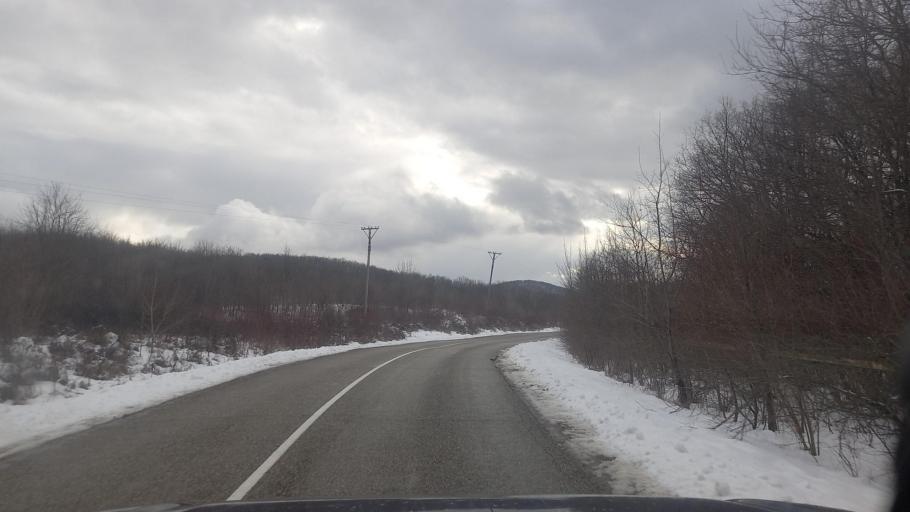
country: RU
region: Krasnodarskiy
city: Smolenskaya
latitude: 44.7343
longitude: 38.8386
